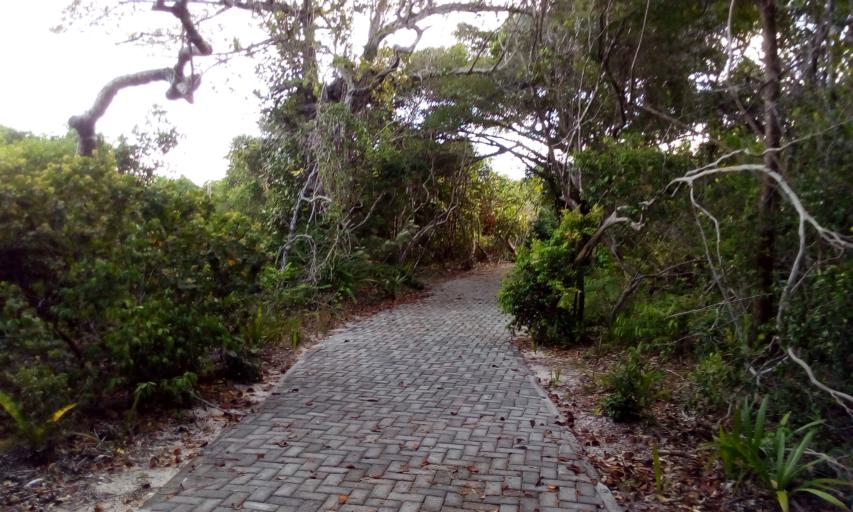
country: BR
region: Bahia
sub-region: Mata De Sao Joao
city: Mata de Sao Joao
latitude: -12.5634
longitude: -37.9990
